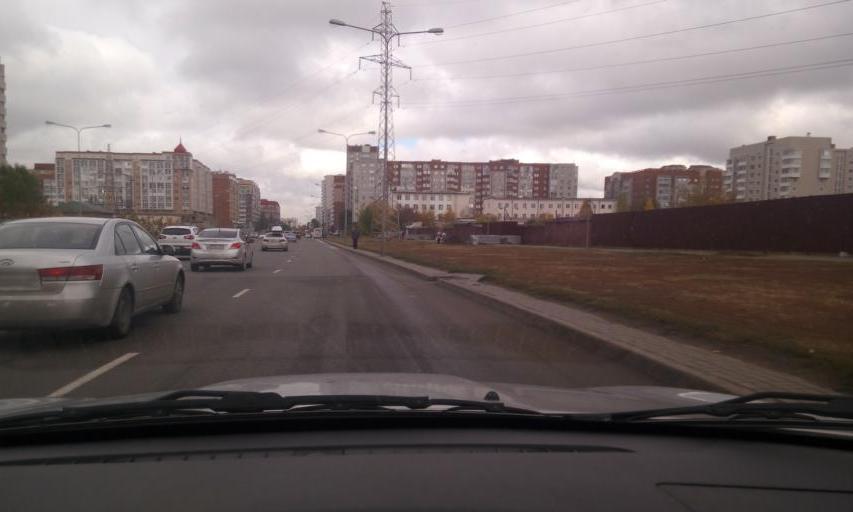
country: KZ
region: Astana Qalasy
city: Astana
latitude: 51.1692
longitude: 71.3951
